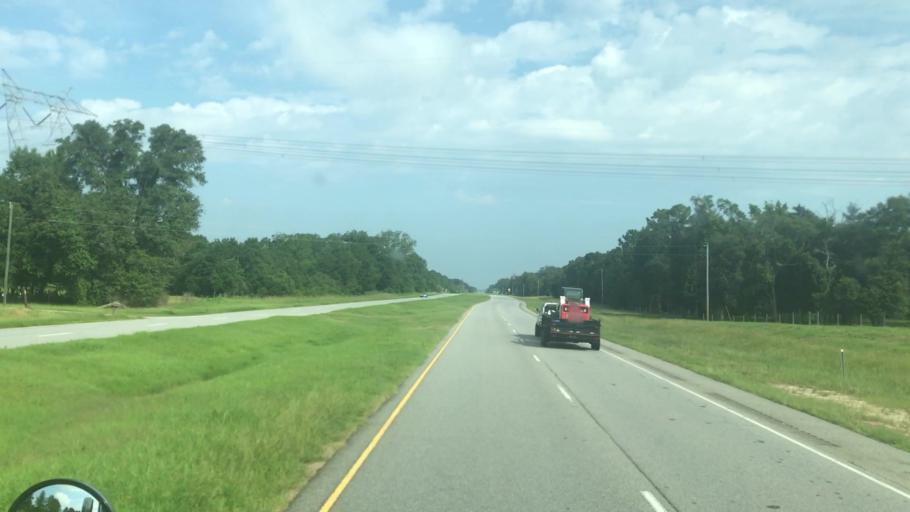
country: US
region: Georgia
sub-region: Early County
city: Blakely
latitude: 31.2844
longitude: -84.8418
